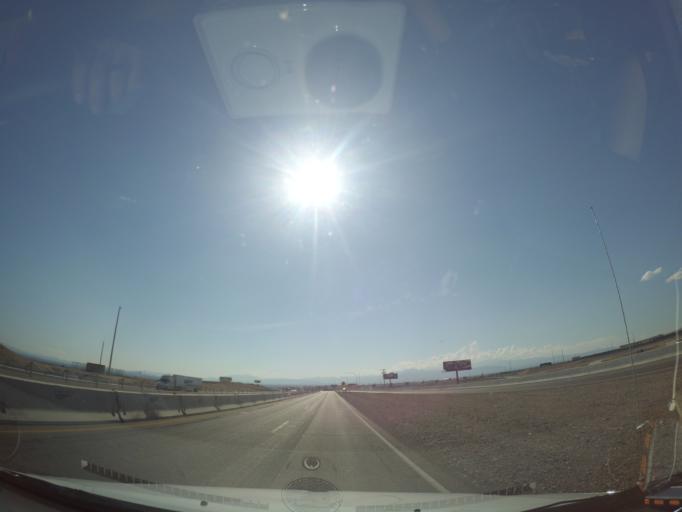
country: US
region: Nevada
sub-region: Clark County
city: Nellis Air Force Base
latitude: 36.2692
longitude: -115.0638
